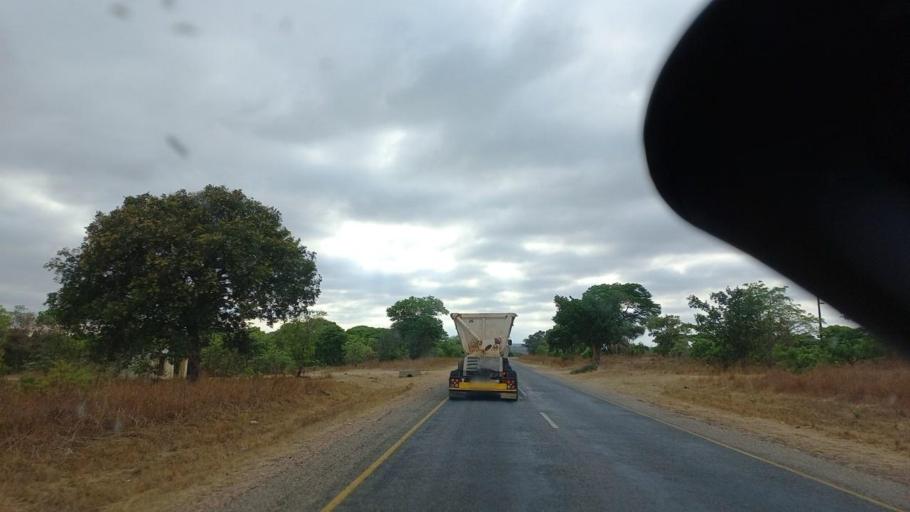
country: ZM
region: Lusaka
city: Chongwe
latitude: -15.2817
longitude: 28.7879
